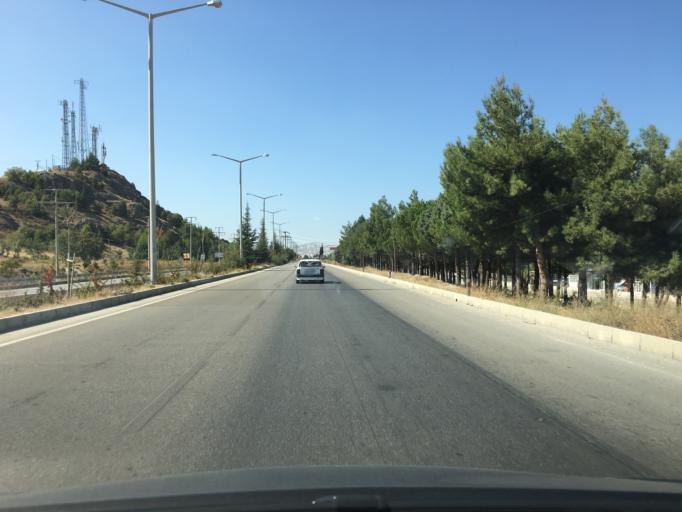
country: TR
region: Burdur
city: Burdur
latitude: 37.7459
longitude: 30.3185
